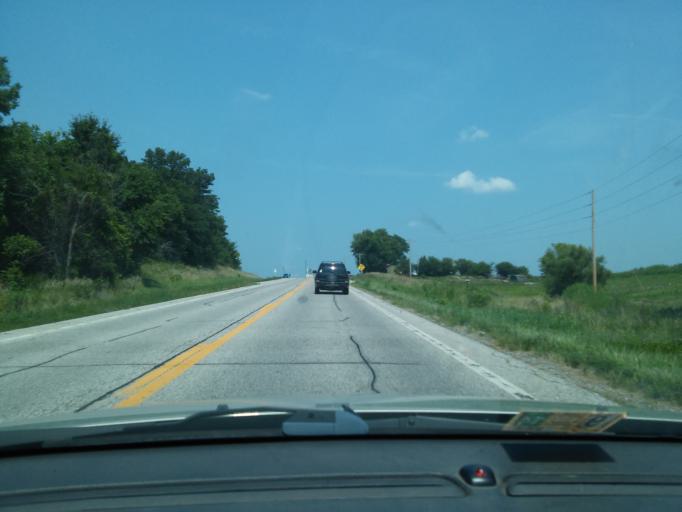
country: US
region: Illinois
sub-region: Pike County
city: Griggsville
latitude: 39.6682
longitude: -90.7704
